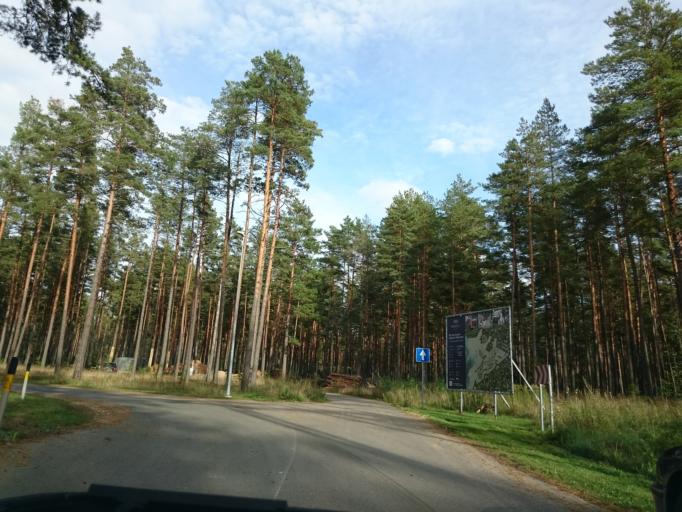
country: LV
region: Adazi
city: Adazi
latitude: 57.0527
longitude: 24.3597
